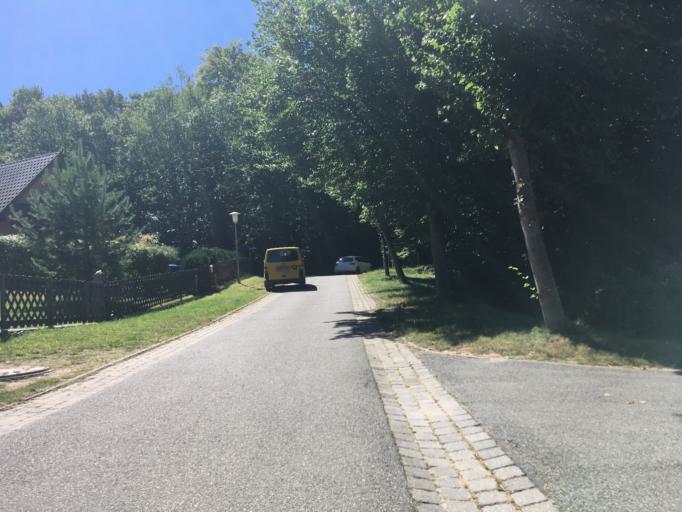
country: DE
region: Brandenburg
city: Grosswoltersdorf
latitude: 53.1445
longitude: 13.0529
